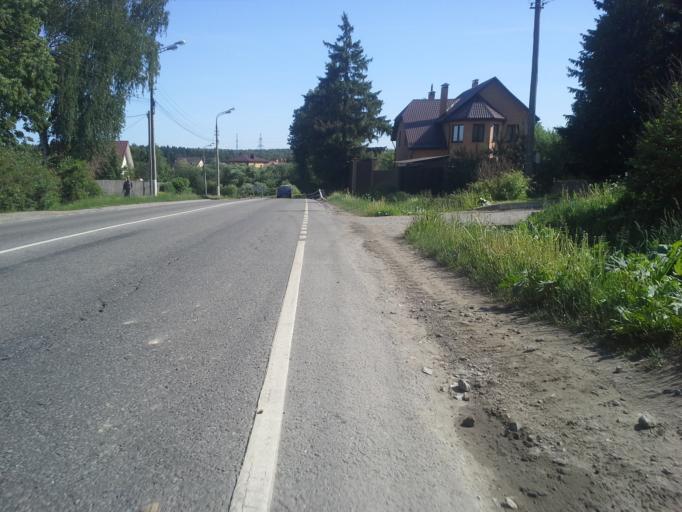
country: RU
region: Moskovskaya
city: Troitsk
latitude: 55.4245
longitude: 37.2814
